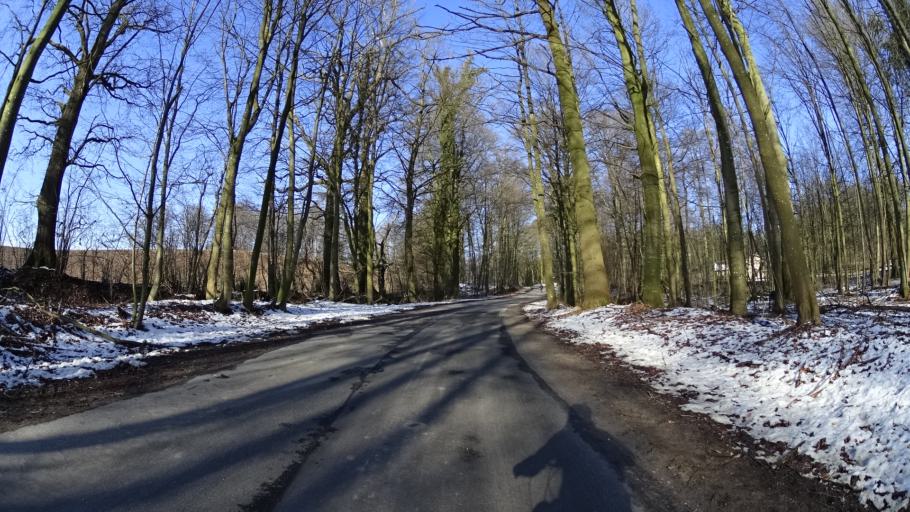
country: DE
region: Schleswig-Holstein
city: Martensrade
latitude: 54.2651
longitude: 10.3887
